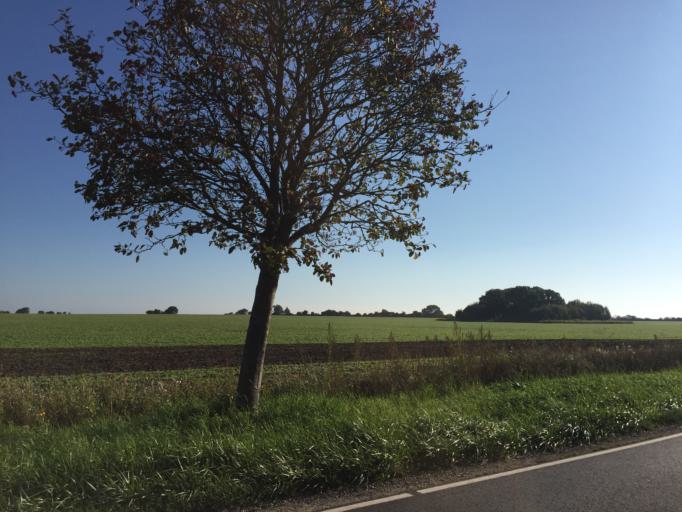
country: DK
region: South Denmark
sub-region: Kerteminde Kommune
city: Kerteminde
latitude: 55.4107
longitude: 10.7149
